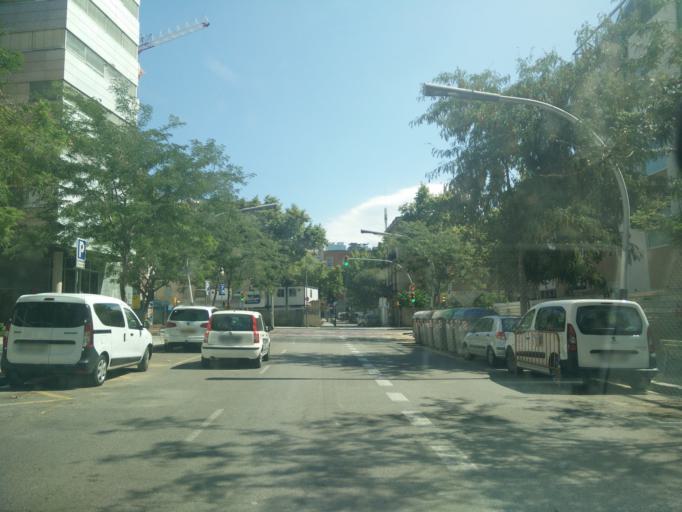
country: ES
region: Catalonia
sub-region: Provincia de Barcelona
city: les Corts
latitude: 41.3878
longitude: 2.1393
